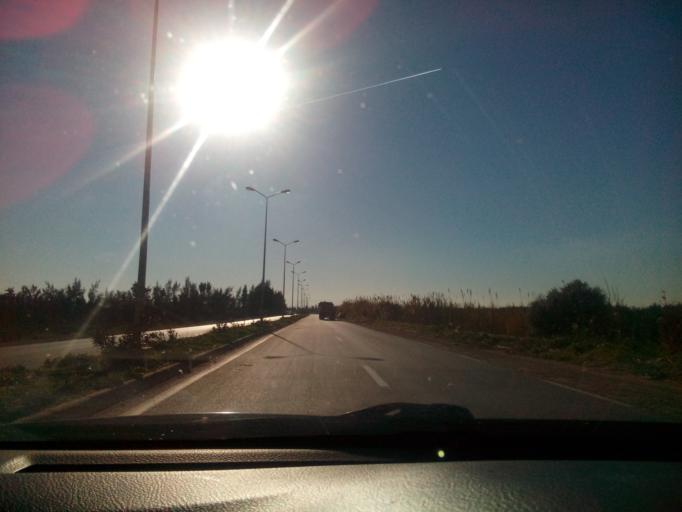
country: DZ
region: Relizane
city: Relizane
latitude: 35.7376
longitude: 0.6027
